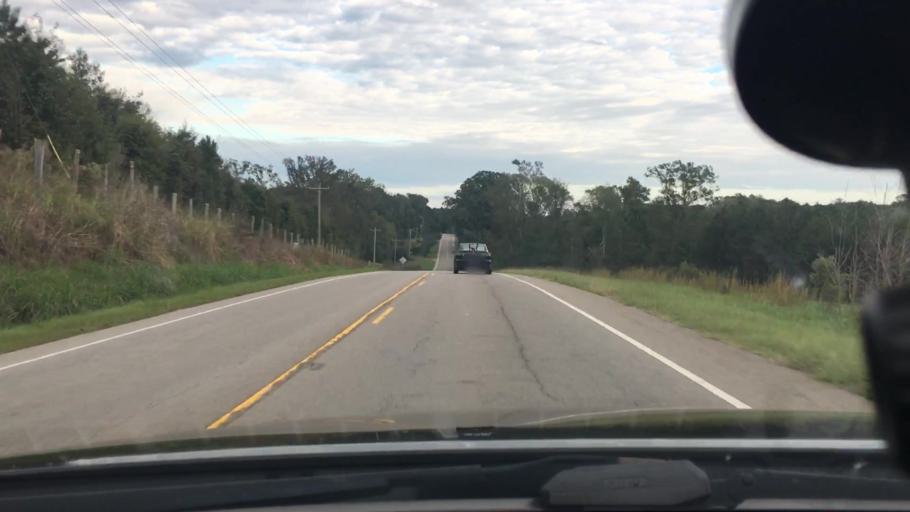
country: US
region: North Carolina
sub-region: Moore County
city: Robbins
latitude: 35.3986
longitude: -79.5466
